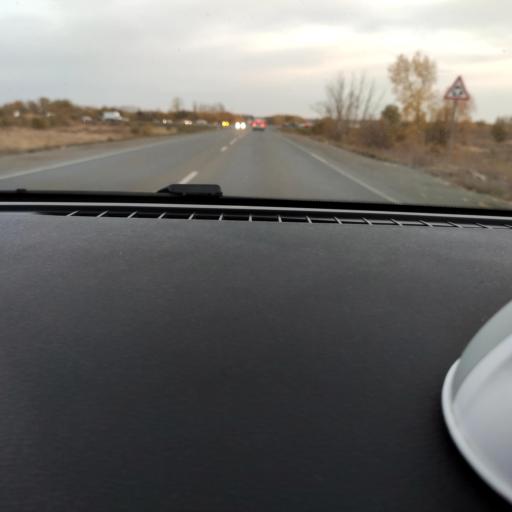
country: RU
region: Samara
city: Samara
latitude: 53.0943
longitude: 50.1486
